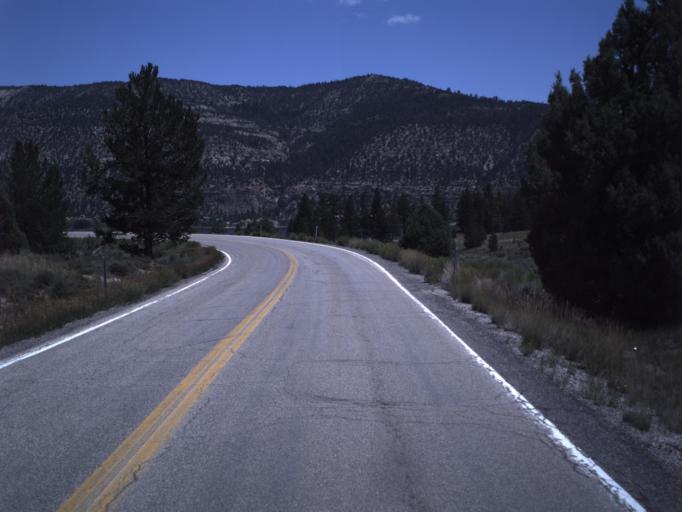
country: US
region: Utah
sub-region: Emery County
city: Orangeville
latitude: 39.2995
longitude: -111.2941
